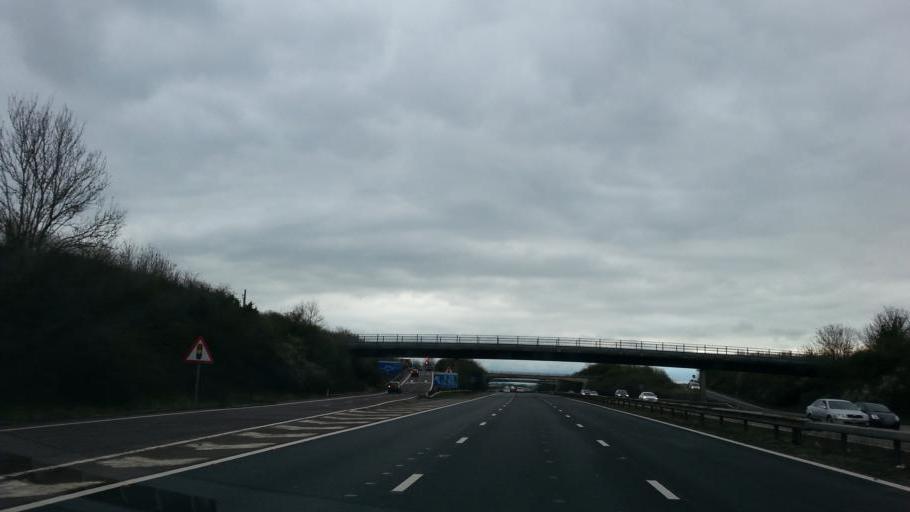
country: GB
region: England
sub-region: Somerset
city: Puriton
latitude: 51.1703
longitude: -2.9799
